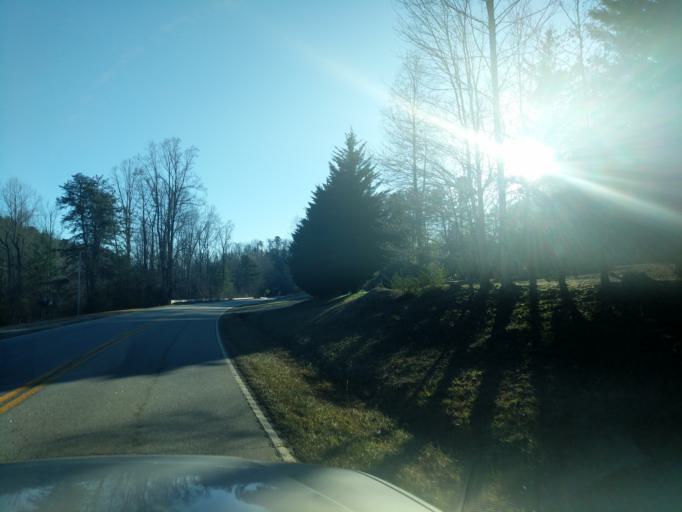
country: US
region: South Carolina
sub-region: Oconee County
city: Westminster
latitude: 34.7452
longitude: -83.2376
